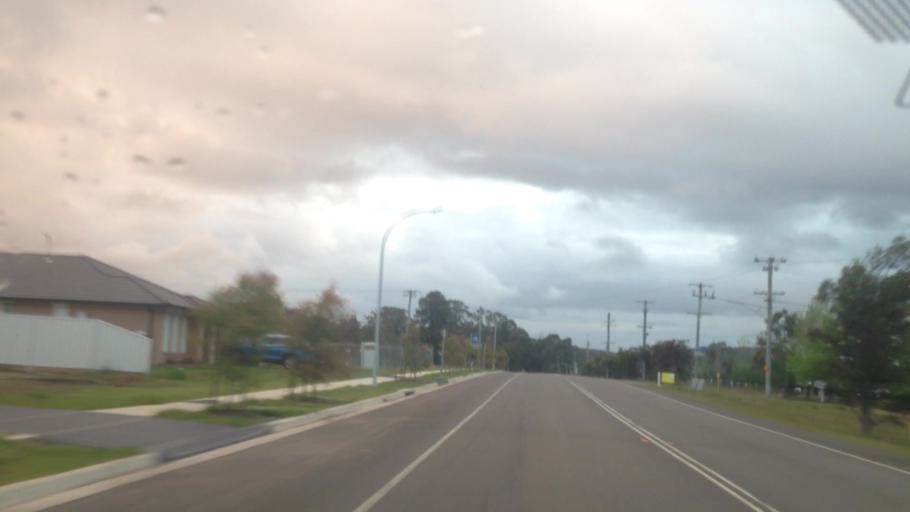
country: AU
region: New South Wales
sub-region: Lake Macquarie Shire
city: Dora Creek
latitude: -33.1045
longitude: 151.4772
